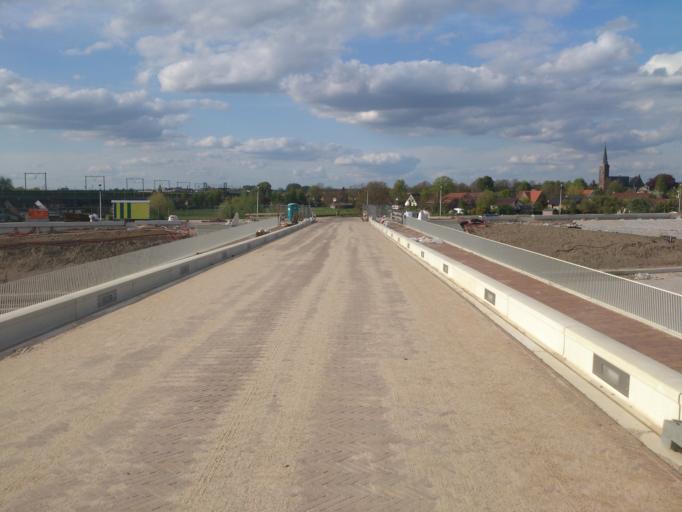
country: NL
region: Gelderland
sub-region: Gemeente Nijmegen
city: Nijmegen
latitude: 51.8562
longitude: 5.8619
